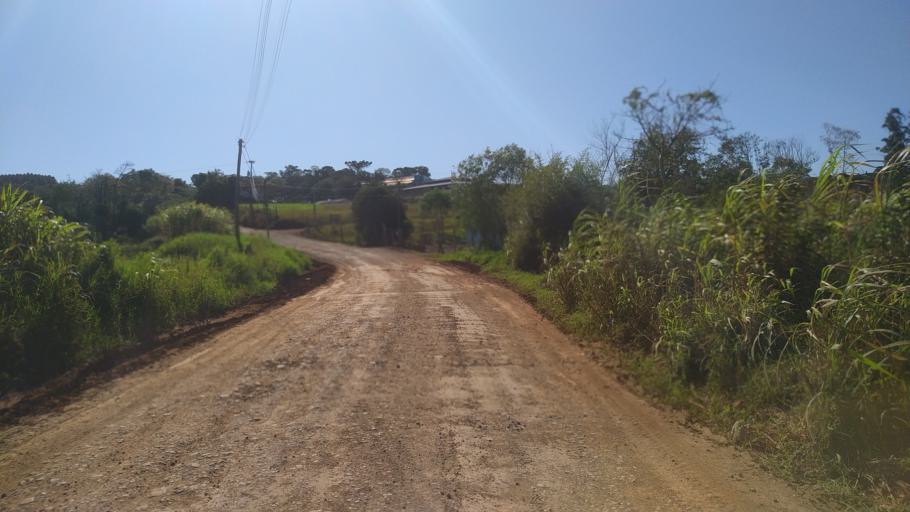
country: BR
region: Santa Catarina
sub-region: Chapeco
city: Chapeco
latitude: -27.1471
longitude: -52.5948
